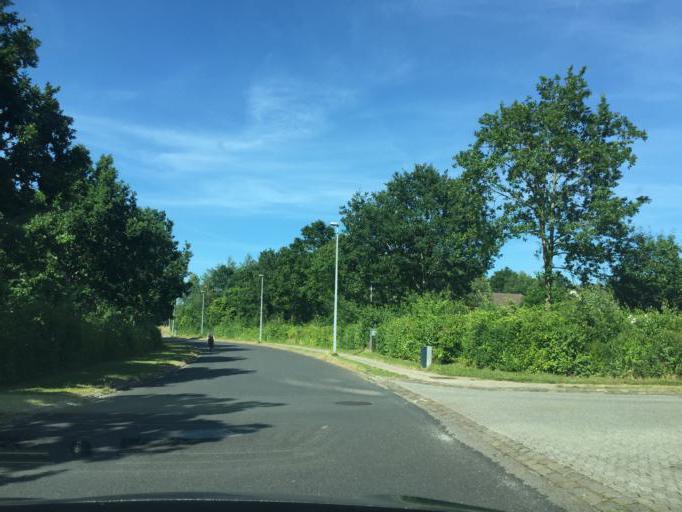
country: DK
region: South Denmark
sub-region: Odense Kommune
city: Neder Holluf
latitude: 55.3736
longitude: 10.4679
